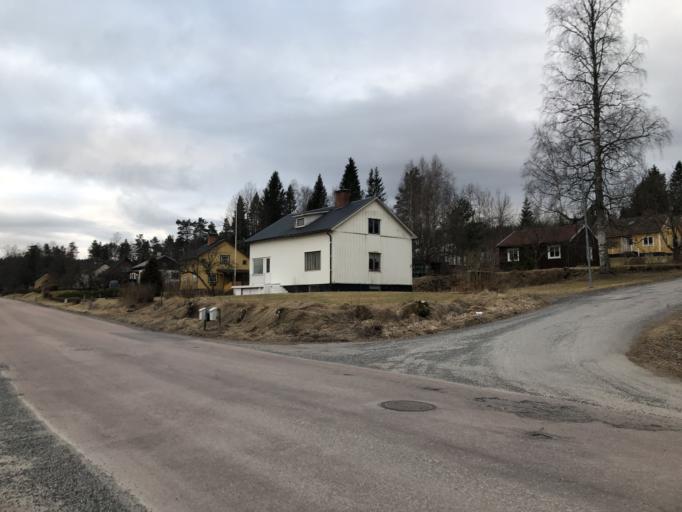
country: SE
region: Vaermland
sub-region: Filipstads Kommun
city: Lesjofors
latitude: 59.9811
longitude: 14.1766
